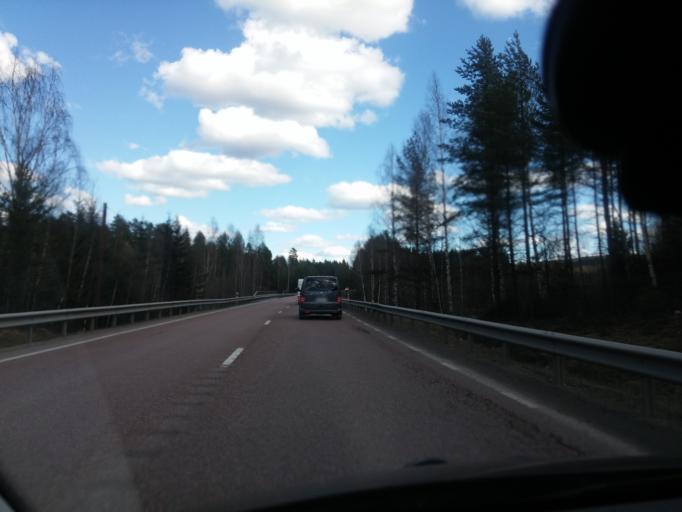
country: SE
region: Gaevleborg
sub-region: Ljusdals Kommun
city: Farila
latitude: 61.8075
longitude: 15.9278
